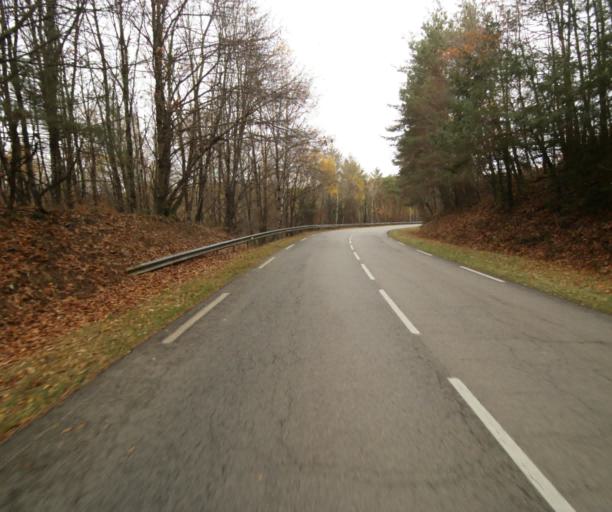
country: FR
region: Limousin
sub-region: Departement de la Correze
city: Sainte-Fortunade
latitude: 45.1822
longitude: 1.7604
